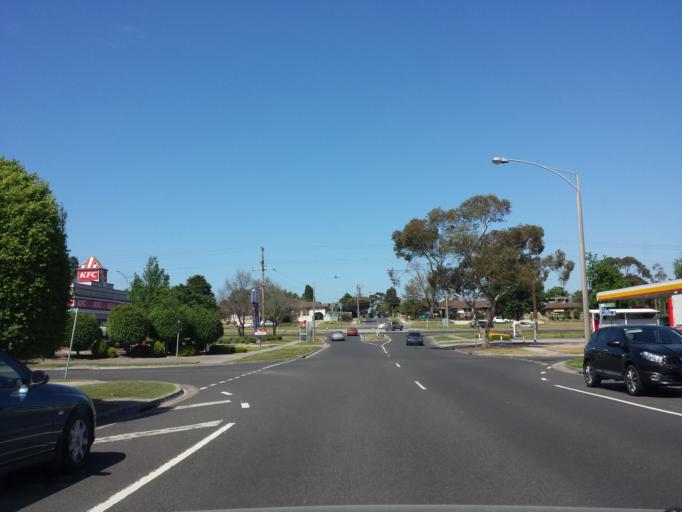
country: AU
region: Victoria
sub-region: Casey
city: Narre Warren
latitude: -38.0257
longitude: 145.3106
